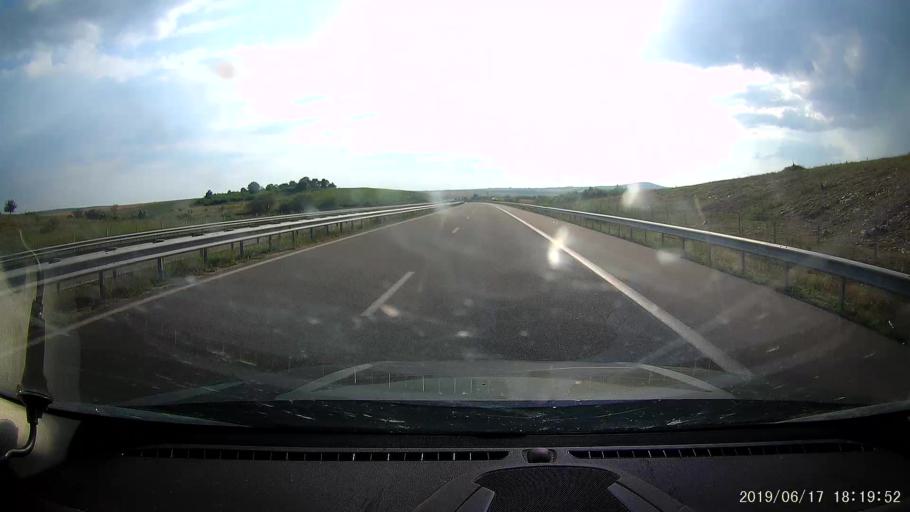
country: BG
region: Khaskovo
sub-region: Obshtina Simeonovgrad
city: Simeonovgrad
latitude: 41.9630
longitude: 25.8326
